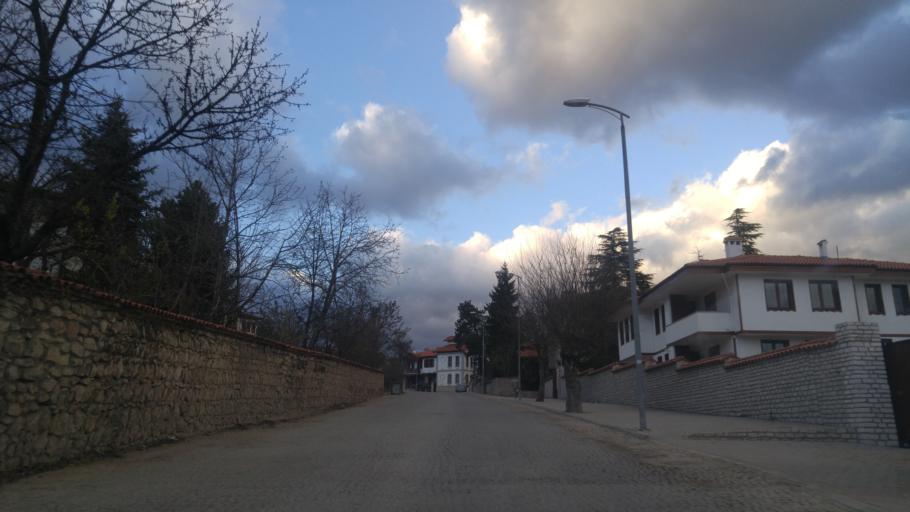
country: TR
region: Karabuk
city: Safranbolu
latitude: 41.2597
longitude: 32.6738
